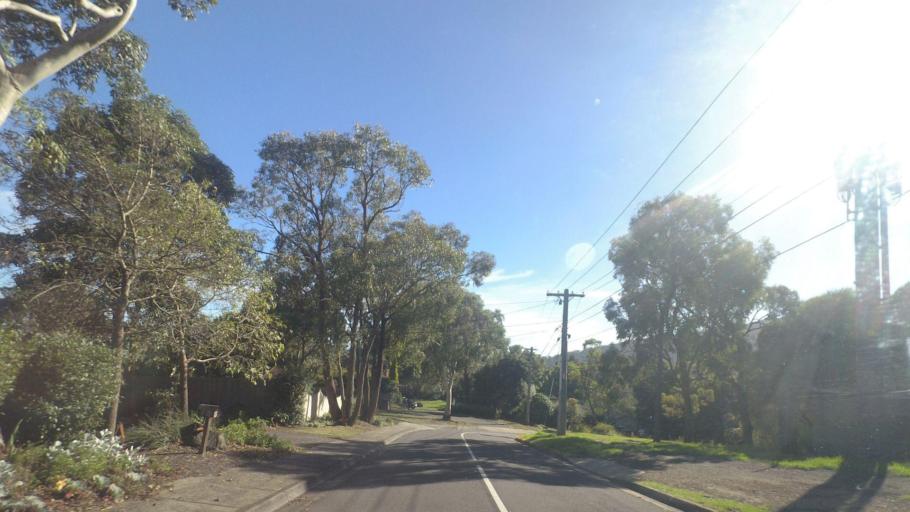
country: AU
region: Victoria
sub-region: Knox
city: Ferntree Gully
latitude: -37.8817
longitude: 145.2907
